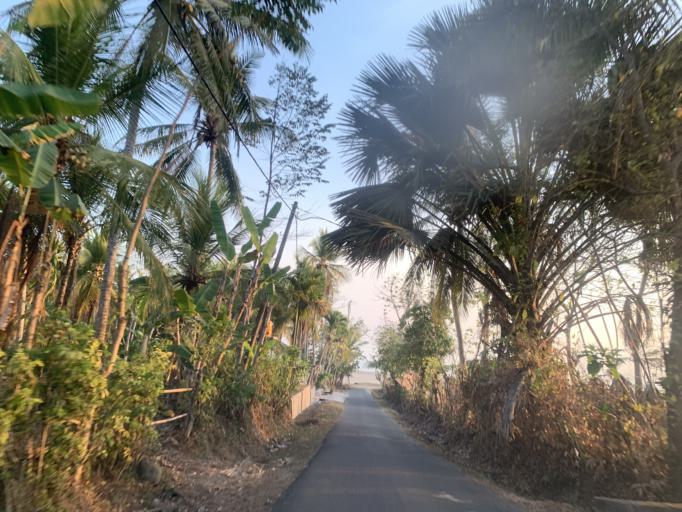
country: ID
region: Bali
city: Banjar Swastika
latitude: -8.4373
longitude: 114.8526
